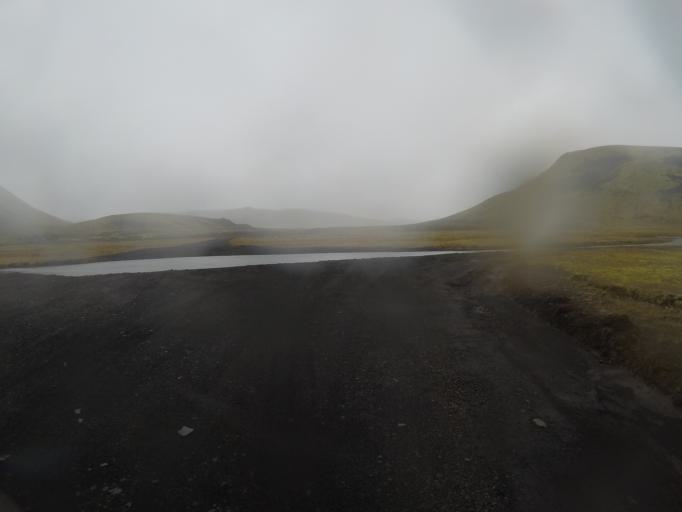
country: IS
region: South
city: Vestmannaeyjar
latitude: 63.9711
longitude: -18.8257
